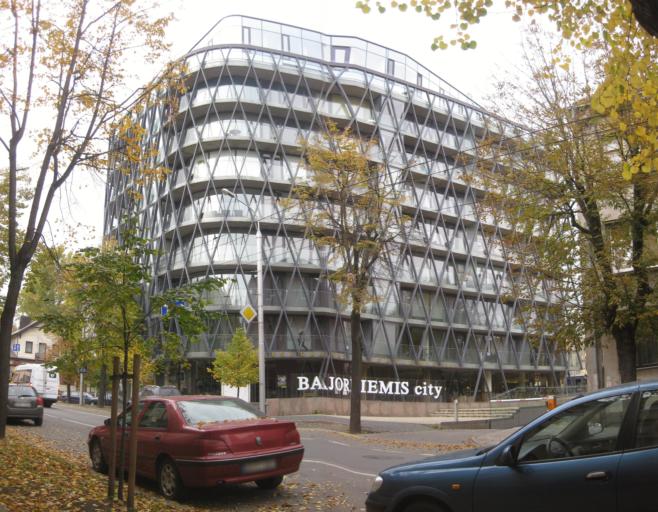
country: LT
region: Kauno apskritis
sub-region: Kaunas
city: Kaunas
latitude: 54.8960
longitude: 23.9040
